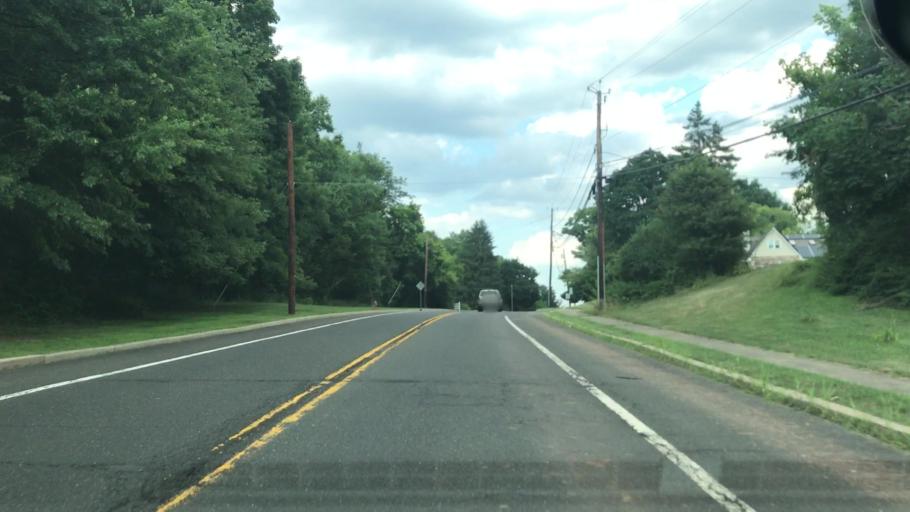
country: US
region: New Jersey
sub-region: Somerset County
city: Bradley Gardens
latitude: 40.5566
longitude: -74.6836
